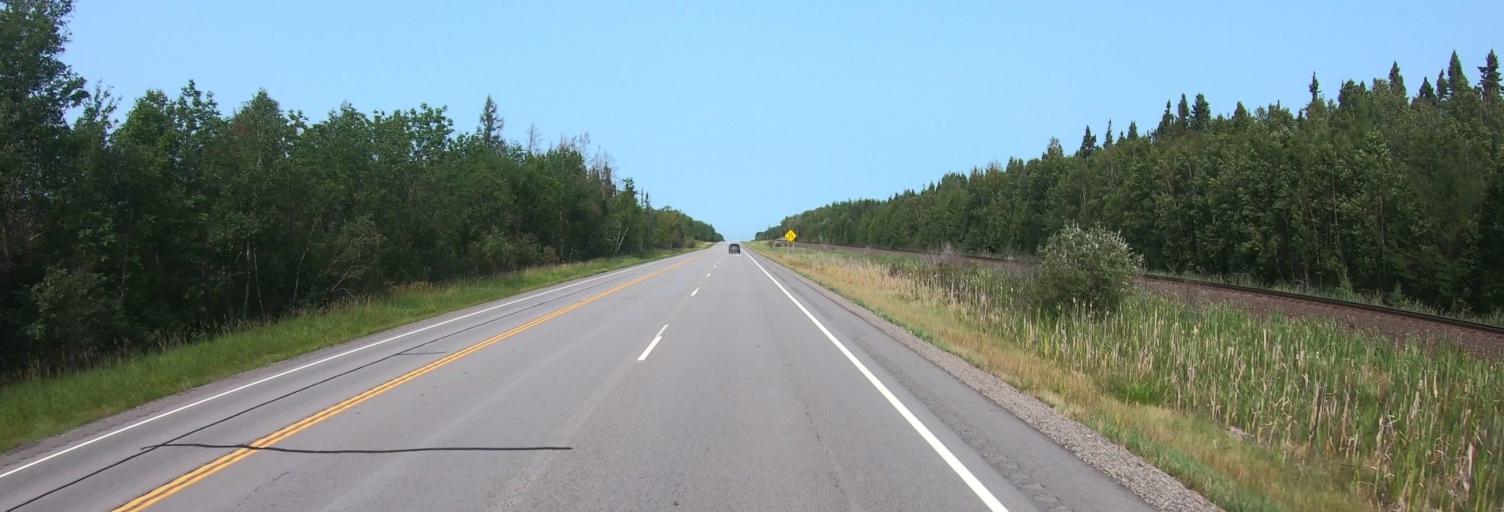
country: CA
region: Ontario
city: Fort Frances
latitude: 48.4581
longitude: -93.2819
